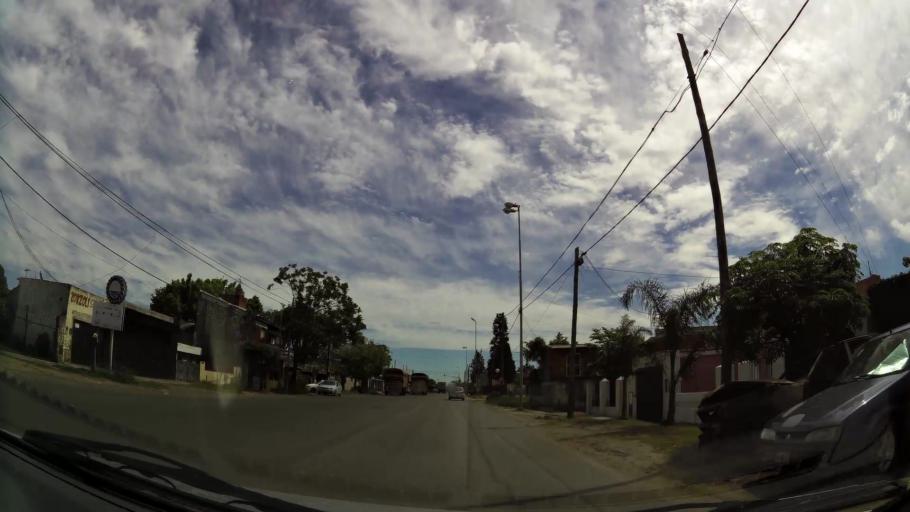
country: AR
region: Buenos Aires
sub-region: Partido de Quilmes
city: Quilmes
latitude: -34.7772
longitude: -58.2870
